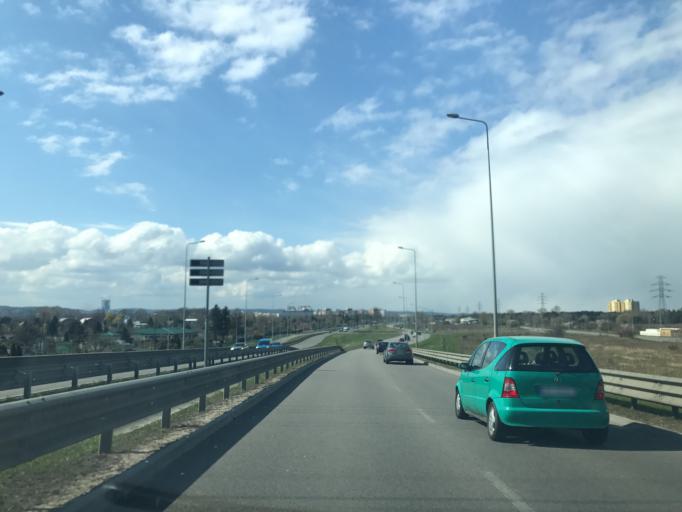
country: PL
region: Pomeranian Voivodeship
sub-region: Gdansk
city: Gdansk
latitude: 54.3948
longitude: 18.6366
